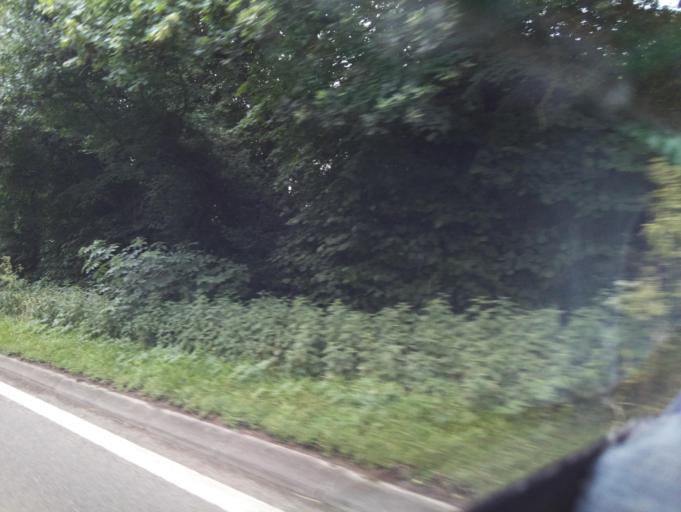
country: GB
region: England
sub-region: Northamptonshire
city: Corby
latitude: 52.5079
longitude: -0.7194
